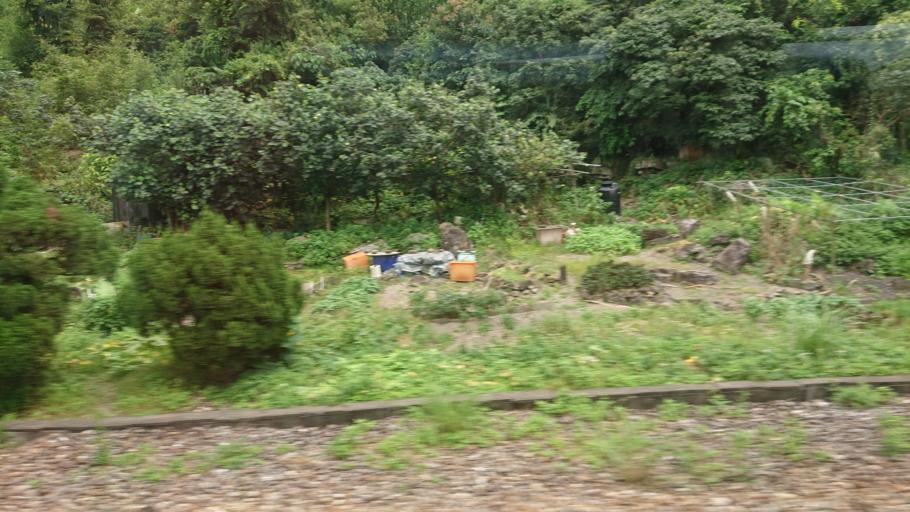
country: TW
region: Taiwan
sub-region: Yilan
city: Yilan
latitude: 24.9393
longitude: 121.8909
